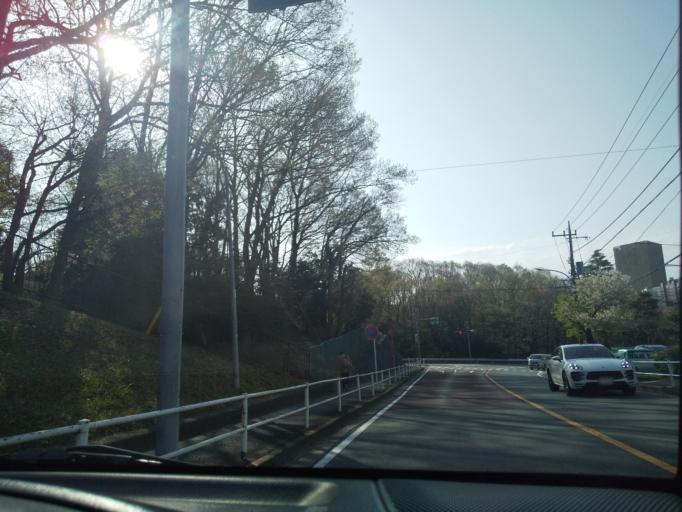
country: JP
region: Tokyo
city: Hino
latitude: 35.6480
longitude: 139.4188
